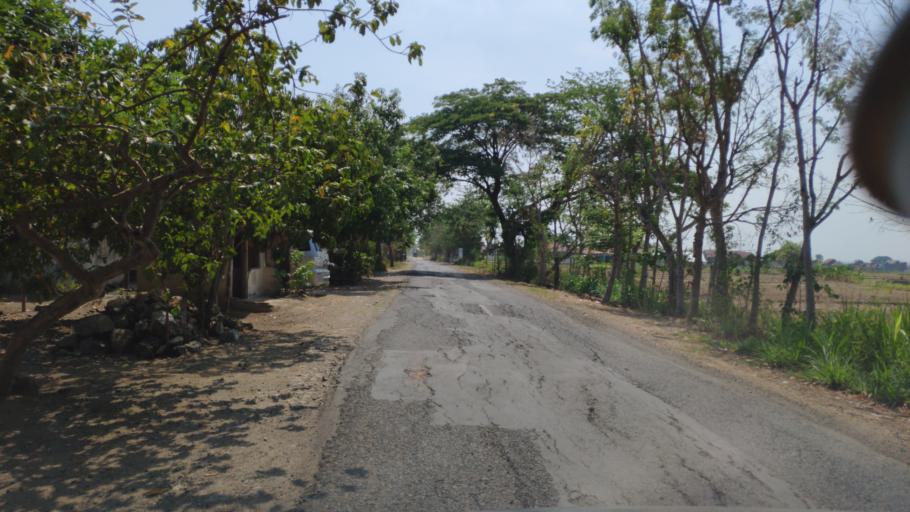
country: ID
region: Central Java
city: Bangkle
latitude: -6.9811
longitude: 111.4321
